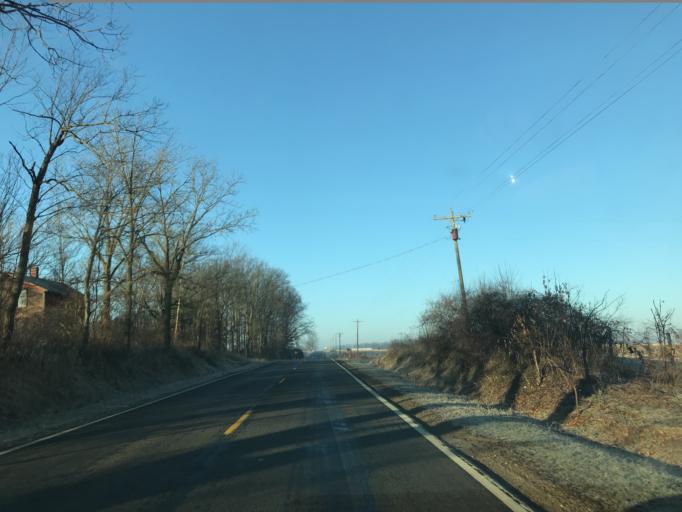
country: US
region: Michigan
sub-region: Eaton County
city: Eaton Rapids
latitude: 42.4511
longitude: -84.5931
